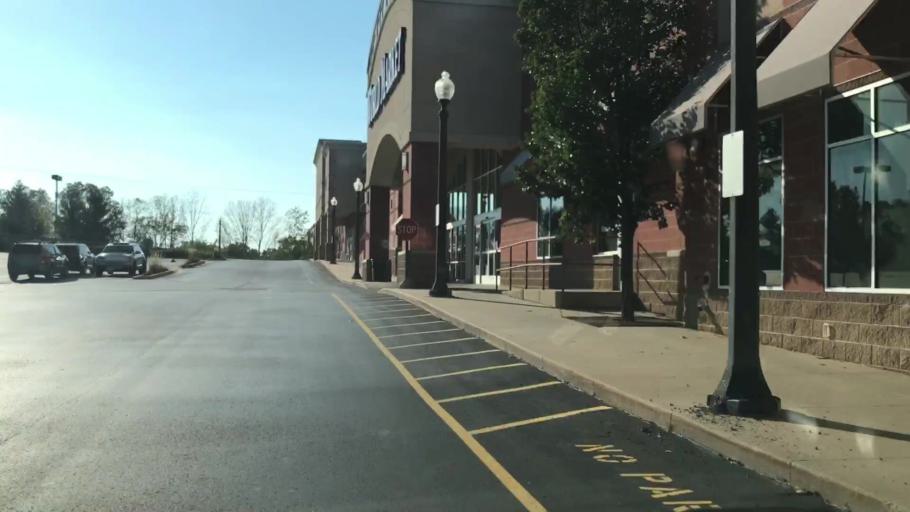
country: US
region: Wisconsin
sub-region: Waukesha County
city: Menomonee Falls
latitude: 43.1929
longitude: -88.1445
